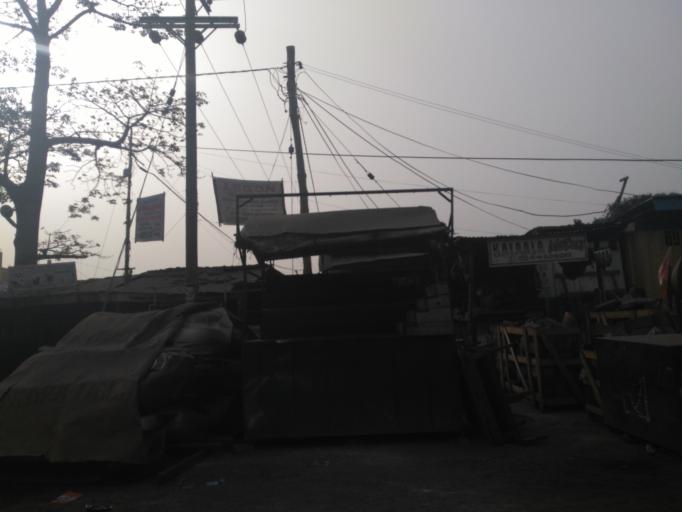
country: GH
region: Ashanti
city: Tafo
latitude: 6.7227
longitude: -1.6333
